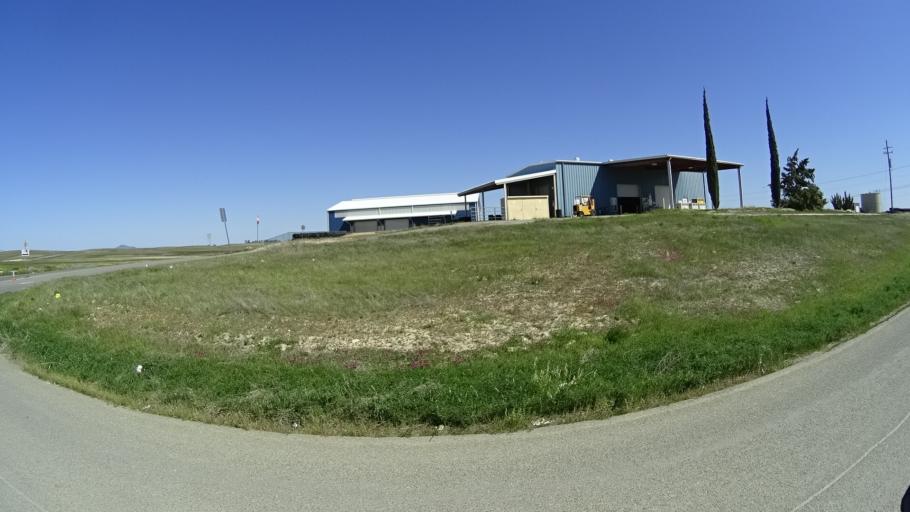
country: US
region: California
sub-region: Glenn County
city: Willows
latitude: 39.6315
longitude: -122.2770
